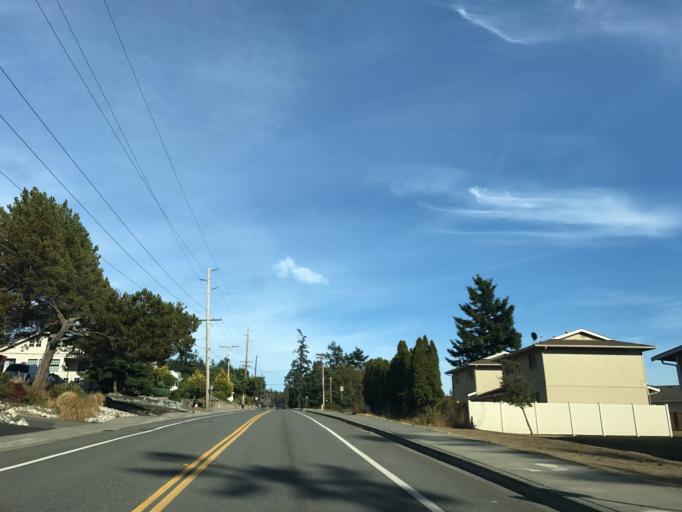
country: US
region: Washington
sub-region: Skagit County
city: Anacortes
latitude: 48.4988
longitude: -122.6876
